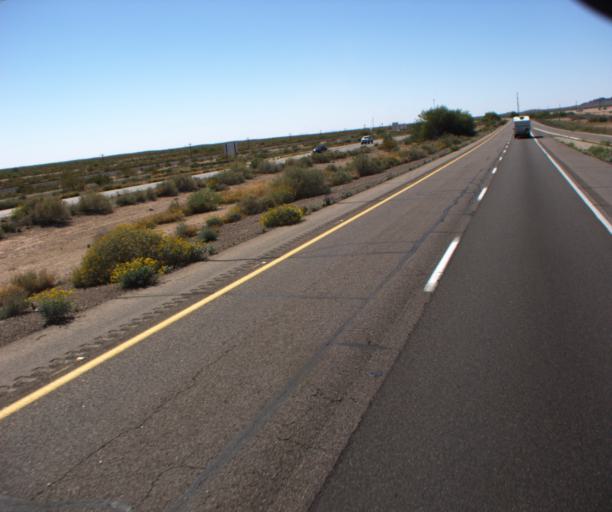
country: US
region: Arizona
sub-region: Maricopa County
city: Gila Bend
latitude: 32.9112
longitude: -112.9624
